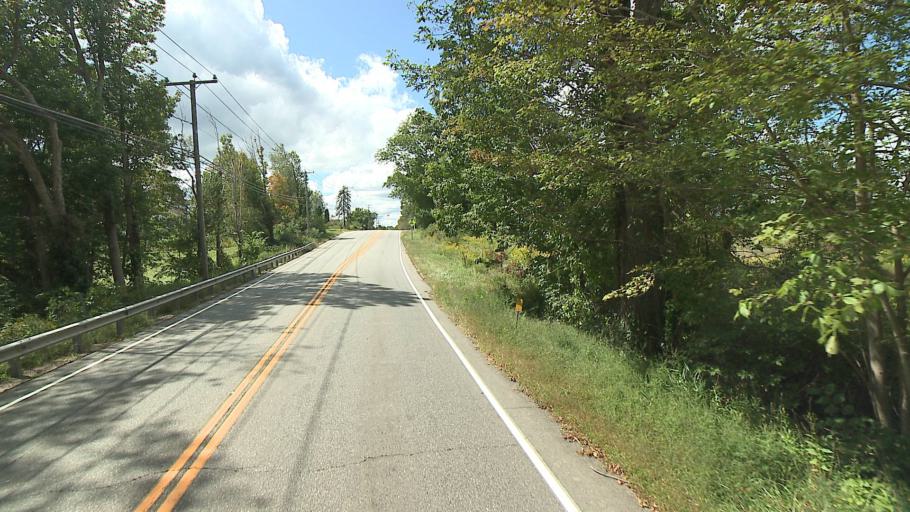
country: US
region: Connecticut
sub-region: Tolland County
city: Storrs
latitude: 41.8741
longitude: -72.1199
